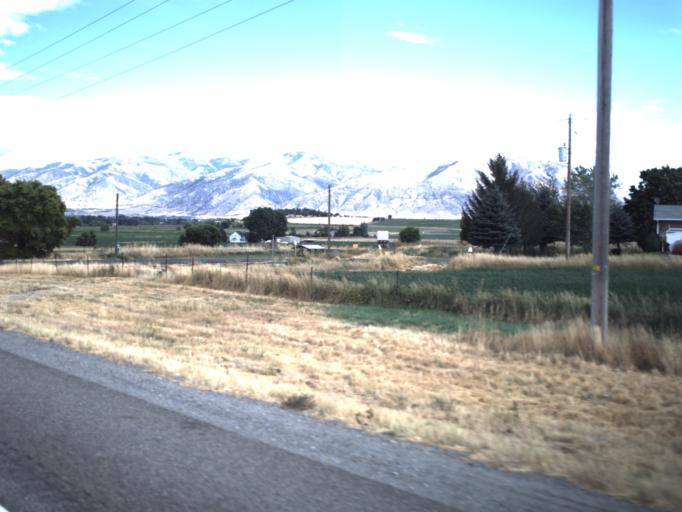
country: US
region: Utah
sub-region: Cache County
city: Wellsville
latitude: 41.6191
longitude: -111.9307
